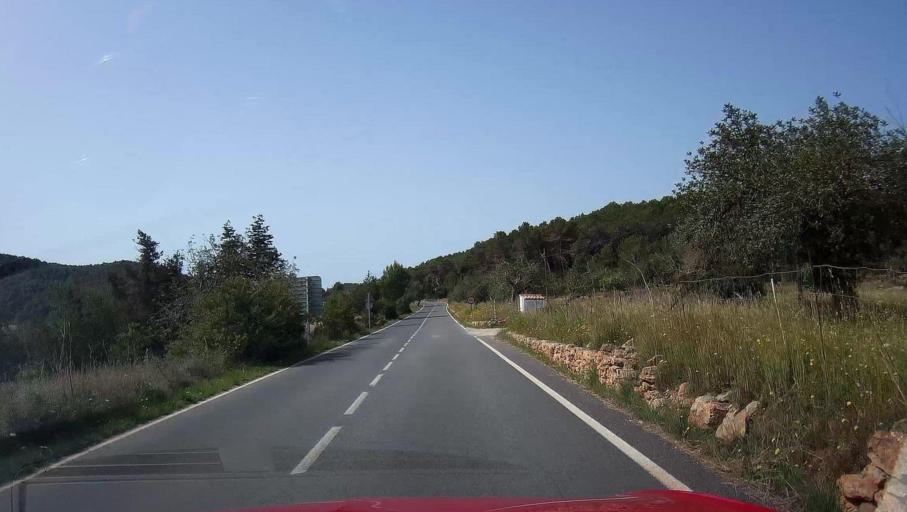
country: ES
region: Balearic Islands
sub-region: Illes Balears
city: Sant Joan de Labritja
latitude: 39.0454
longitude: 1.5686
